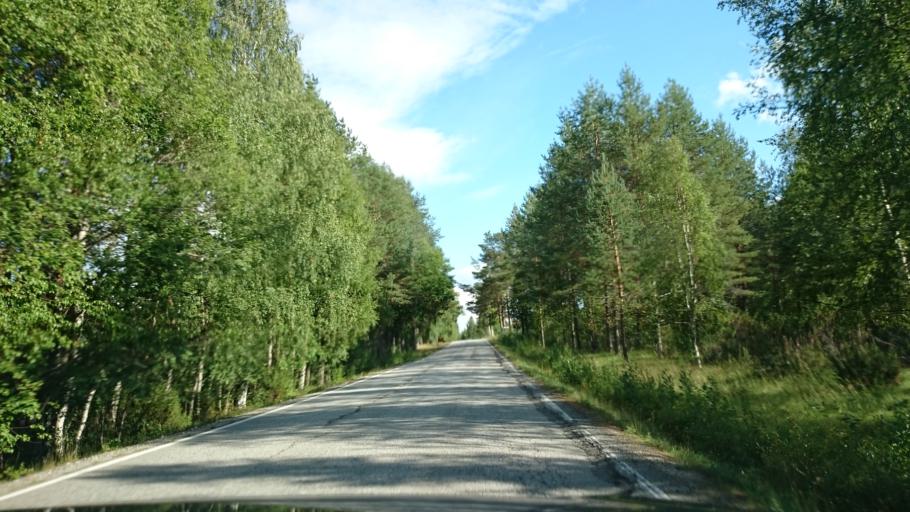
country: FI
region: Kainuu
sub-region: Kehys-Kainuu
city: Suomussalmi
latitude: 64.7603
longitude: 29.3843
